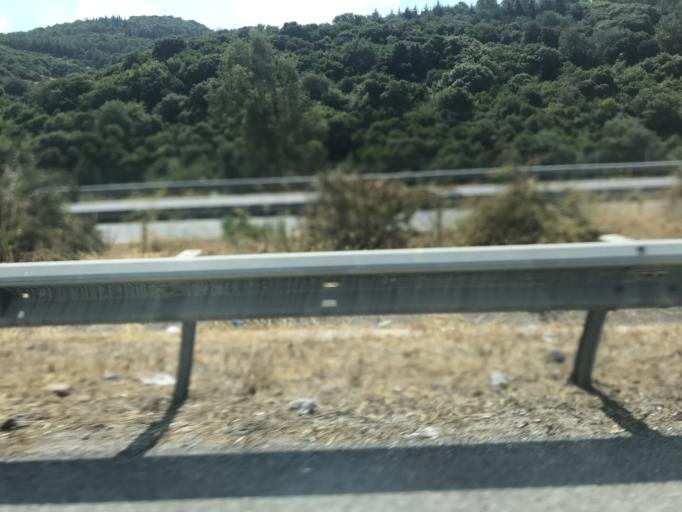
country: TR
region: Izmir
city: Urla
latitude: 38.3802
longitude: 26.9387
